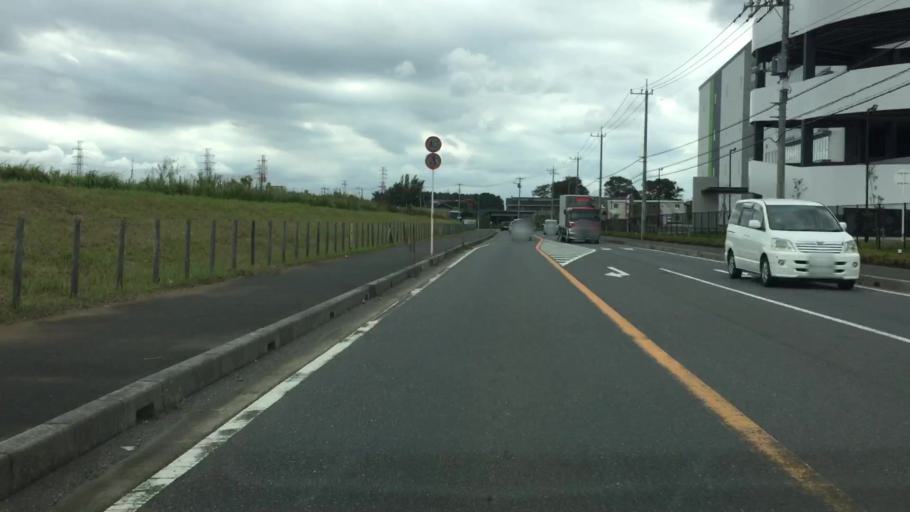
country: JP
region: Chiba
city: Shiroi
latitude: 35.8145
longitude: 140.1334
